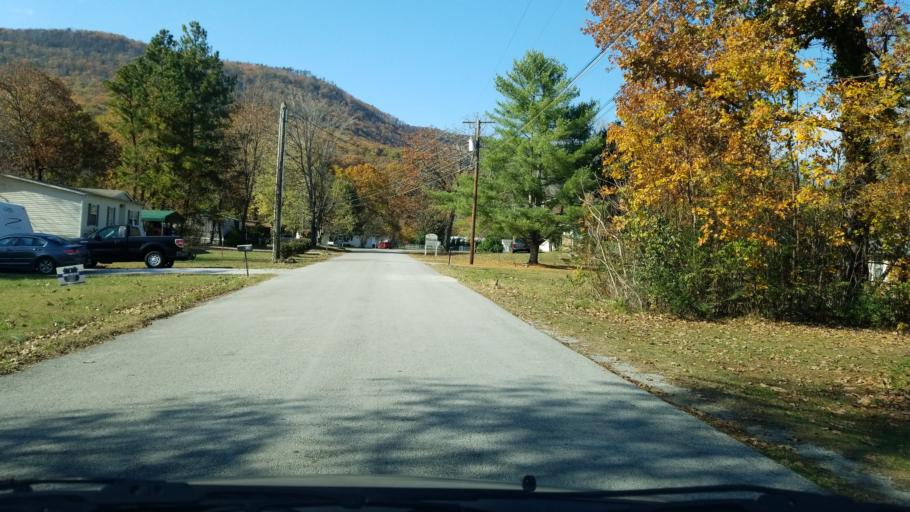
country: US
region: Tennessee
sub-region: Hamilton County
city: Falling Water
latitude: 35.2210
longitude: -85.2256
